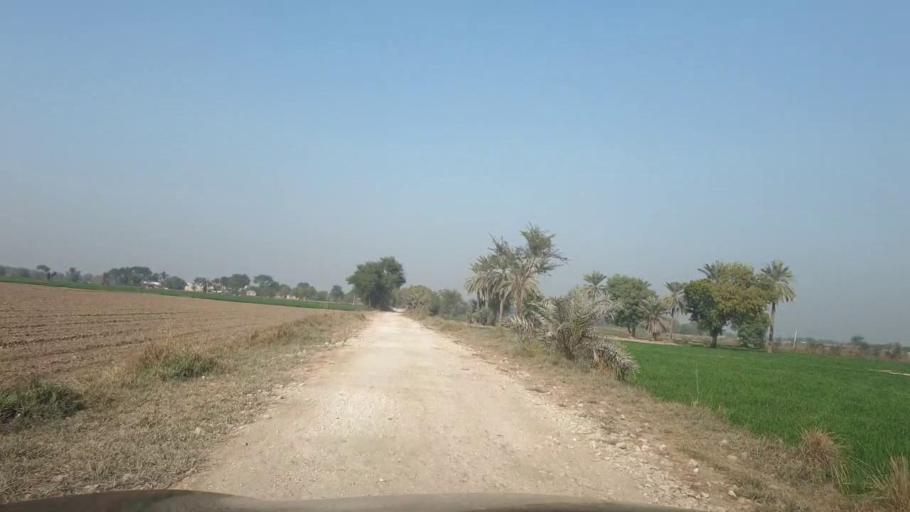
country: PK
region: Sindh
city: Ubauro
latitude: 28.0912
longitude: 69.8412
